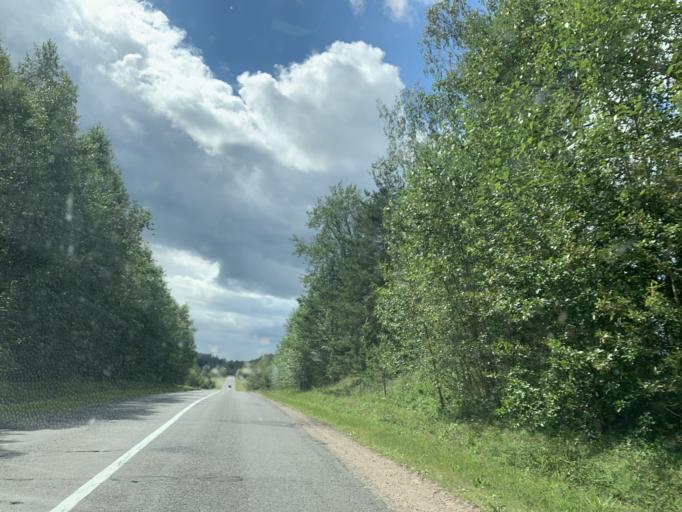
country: BY
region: Minsk
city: Ivyanyets
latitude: 53.9734
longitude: 26.8578
